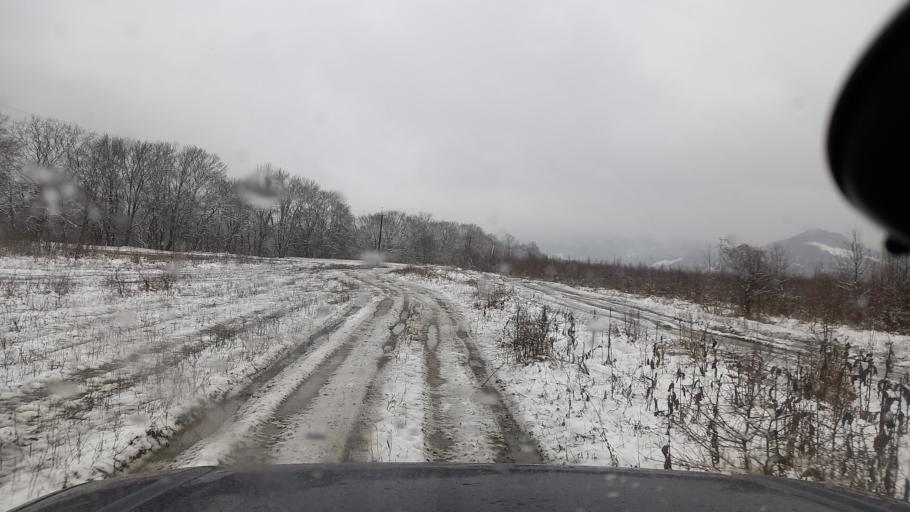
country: RU
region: Adygeya
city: Kamennomostskiy
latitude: 44.2185
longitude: 40.1778
